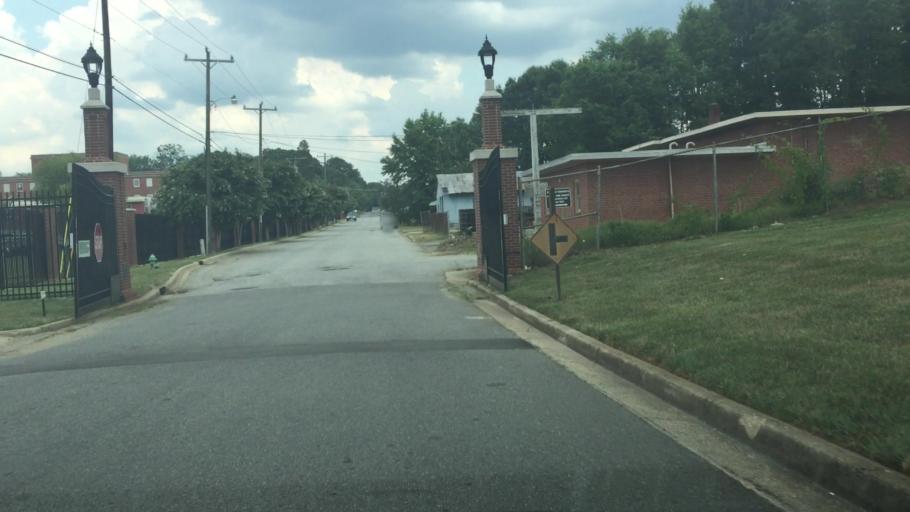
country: US
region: North Carolina
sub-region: Rowan County
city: Salisbury
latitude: 35.6813
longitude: -80.4906
